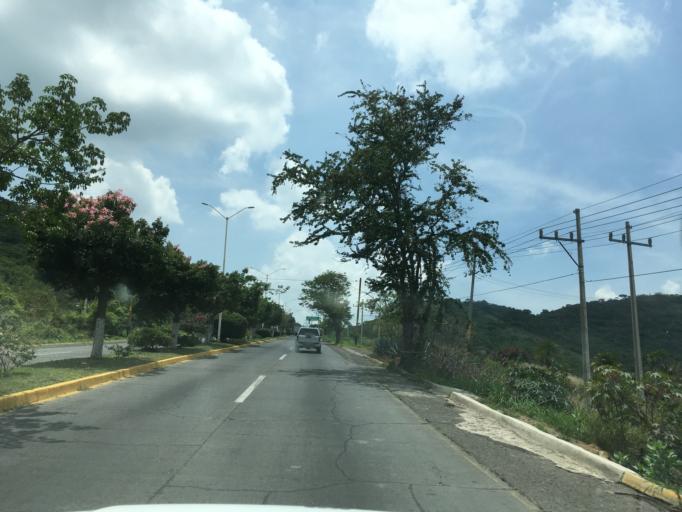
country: MX
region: Jalisco
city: Tlajomulco de Zuniga
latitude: 20.4903
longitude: -103.4710
